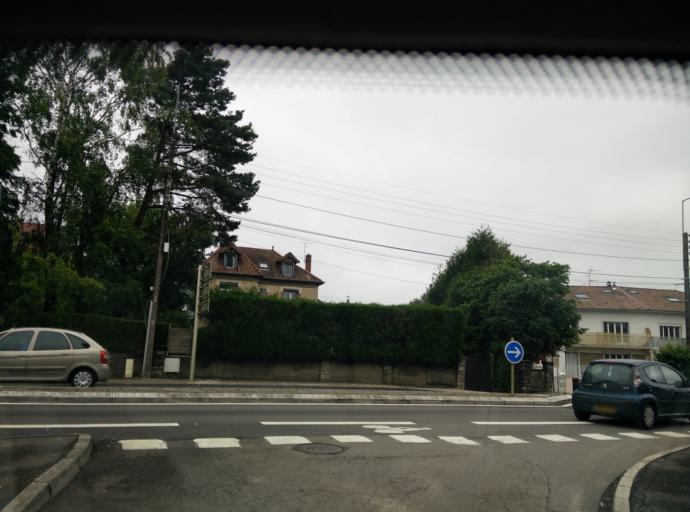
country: FR
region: Franche-Comte
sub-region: Departement du Doubs
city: Beure
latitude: 47.2275
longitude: 5.9826
